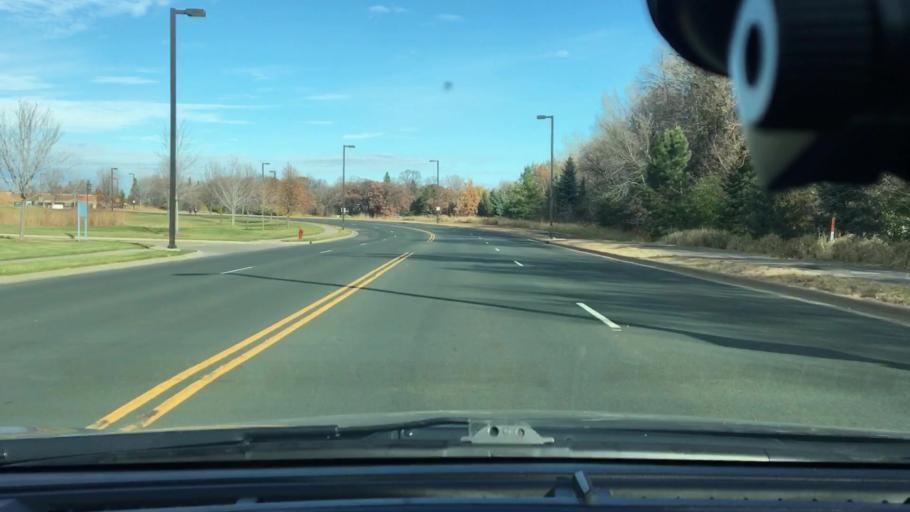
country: US
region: Minnesota
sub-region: Hennepin County
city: Maple Grove
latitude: 45.0761
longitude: -93.4417
